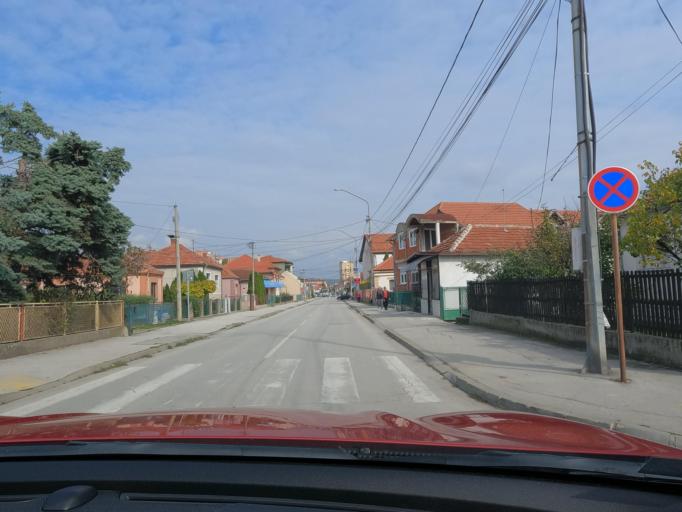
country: RS
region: Central Serbia
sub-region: Moravicki Okrug
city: Cacak
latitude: 43.8823
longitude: 20.3404
